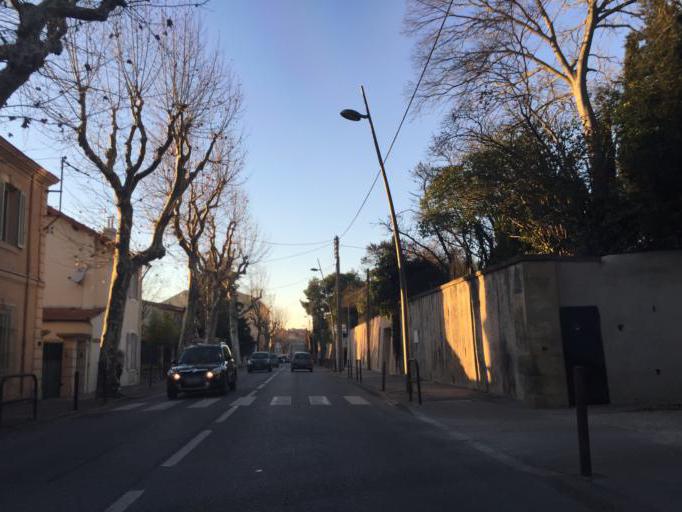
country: FR
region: Provence-Alpes-Cote d'Azur
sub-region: Departement des Bouches-du-Rhone
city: Aix-en-Provence
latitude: 43.5213
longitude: 5.4587
